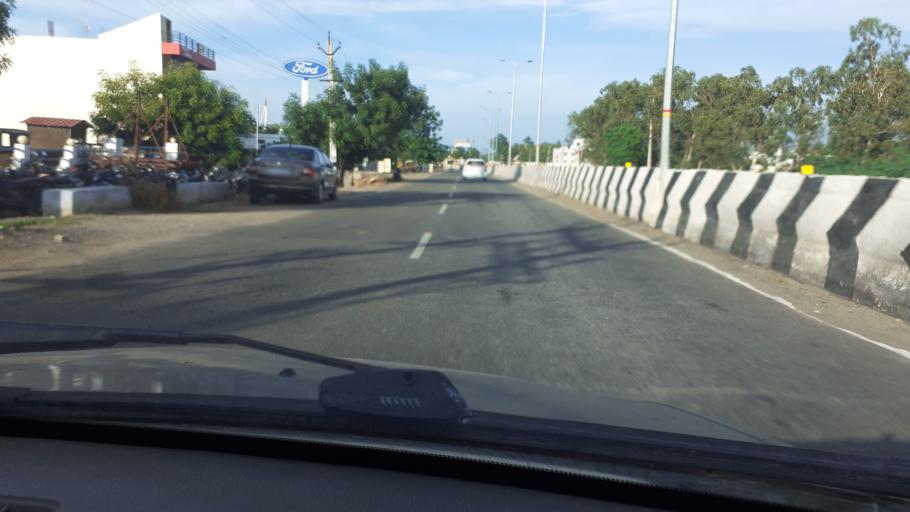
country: IN
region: Tamil Nadu
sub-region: Tirunelveli Kattabo
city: Tirunelveli
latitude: 8.6769
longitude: 77.7217
